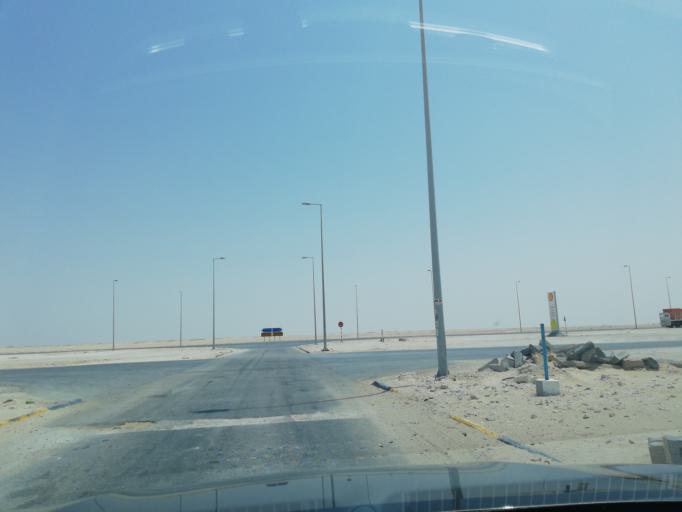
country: OM
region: Al Wusta
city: Hayma'
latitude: 19.6116
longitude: 55.5169
